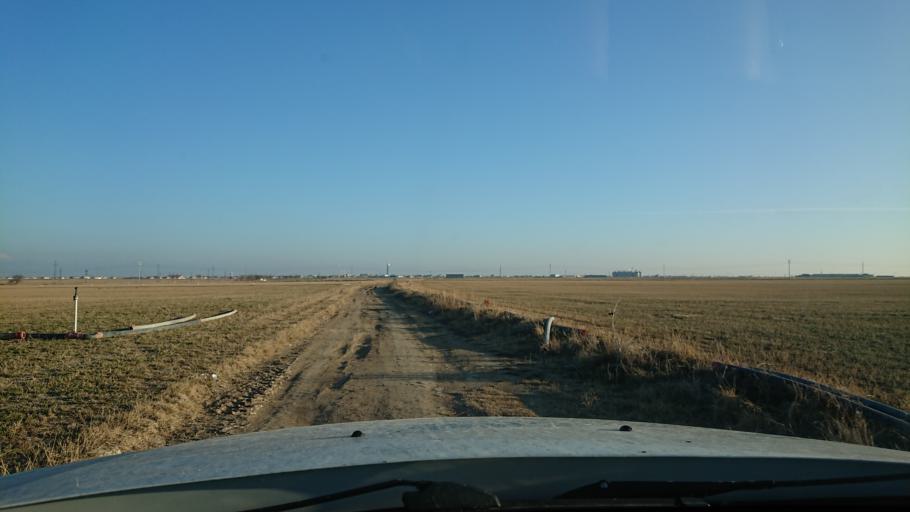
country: TR
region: Aksaray
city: Sultanhani
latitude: 38.2683
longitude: 33.5184
